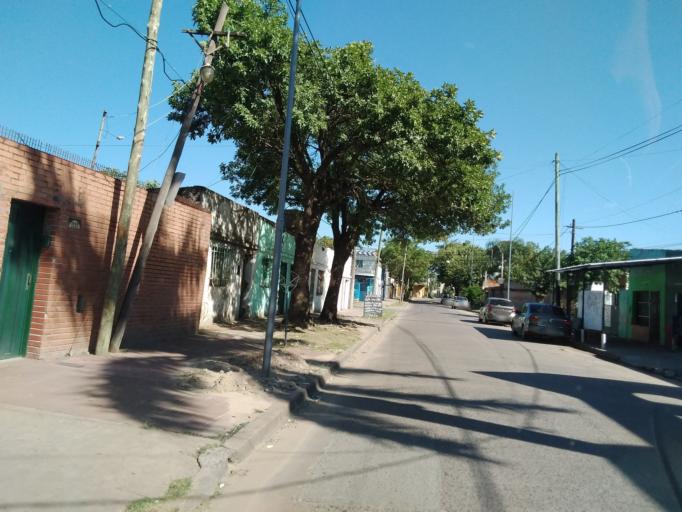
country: AR
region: Corrientes
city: Corrientes
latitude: -27.4798
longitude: -58.8076
